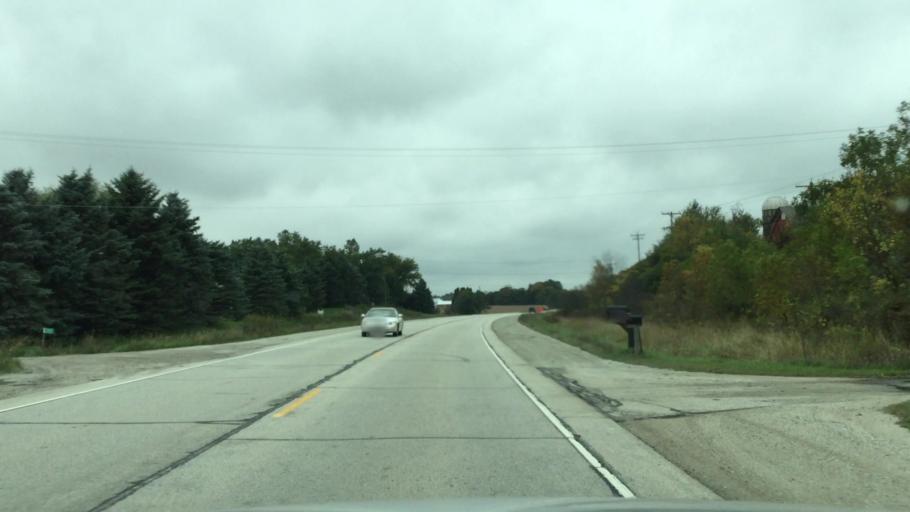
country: US
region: Wisconsin
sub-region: Racine County
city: Union Grove
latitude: 42.7330
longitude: -88.0052
